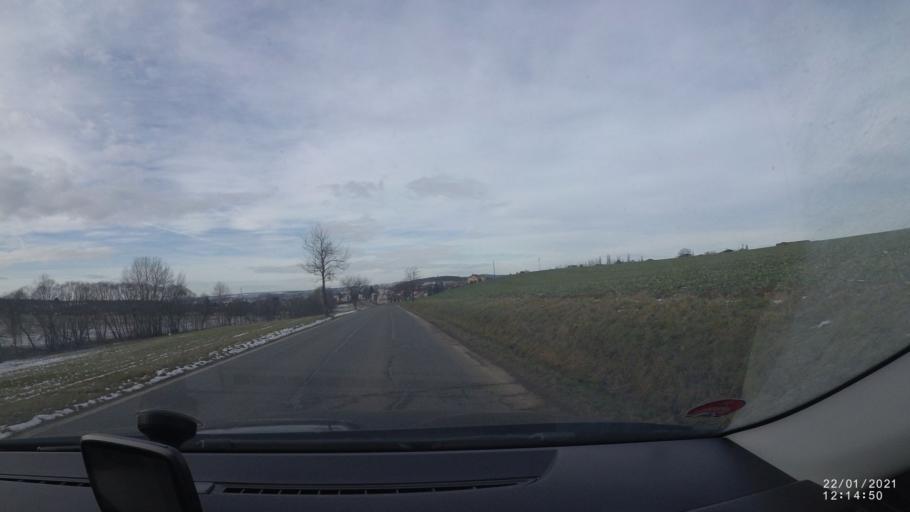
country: CZ
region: Plzensky
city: Dysina
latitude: 49.7570
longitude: 13.4674
